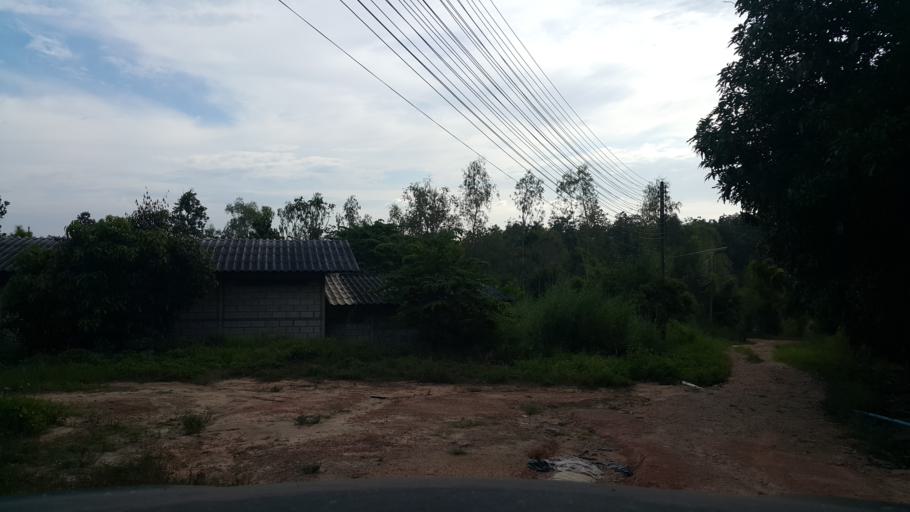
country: TH
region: Chiang Mai
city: San Sai
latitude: 18.9307
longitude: 99.0661
